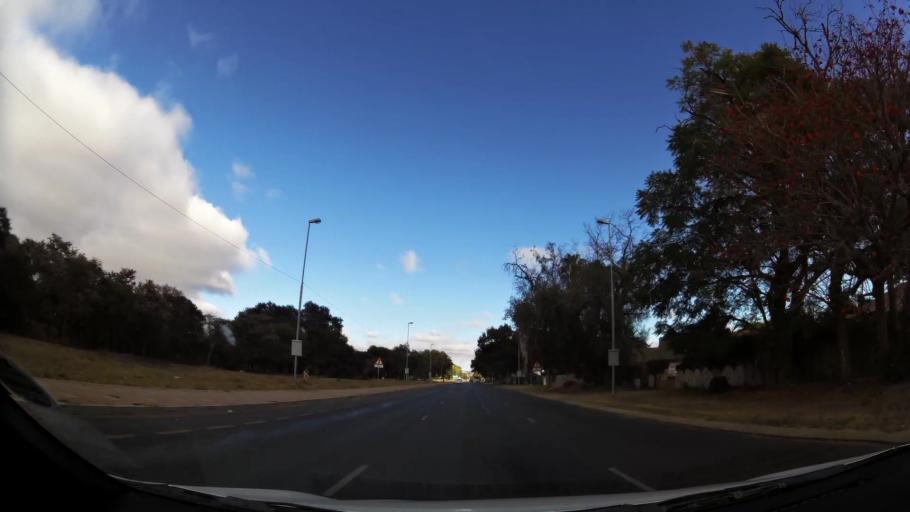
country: ZA
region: Limpopo
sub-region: Capricorn District Municipality
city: Polokwane
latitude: -23.9180
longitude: 29.4667
